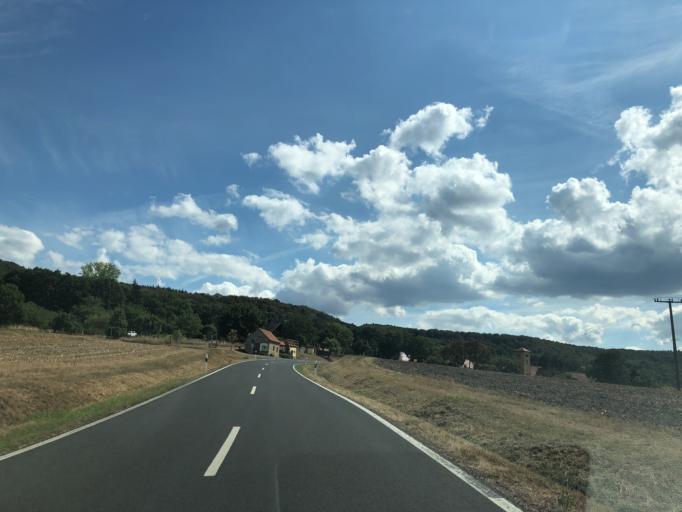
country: DE
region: Bavaria
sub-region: Regierungsbezirk Unterfranken
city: Oberschwarzach
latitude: 49.8305
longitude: 10.4378
